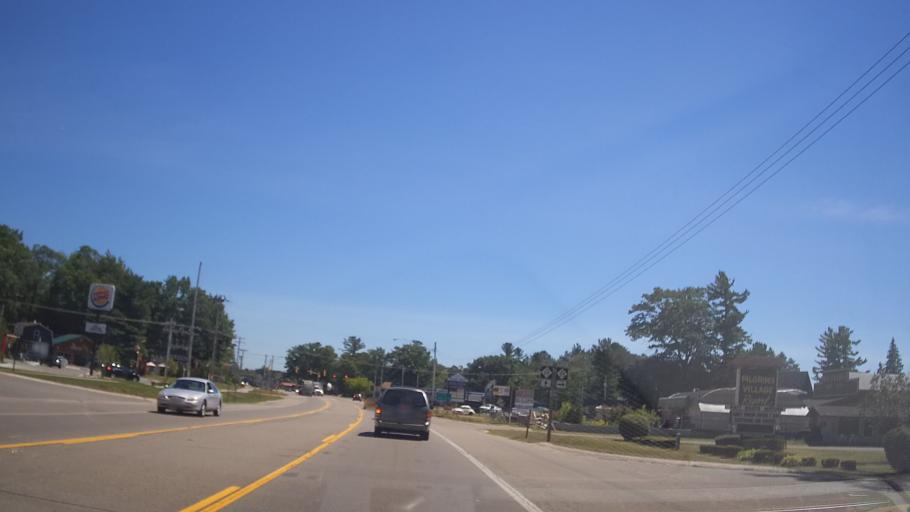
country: US
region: Michigan
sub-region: Wexford County
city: Cadillac
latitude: 44.2375
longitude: -85.4545
